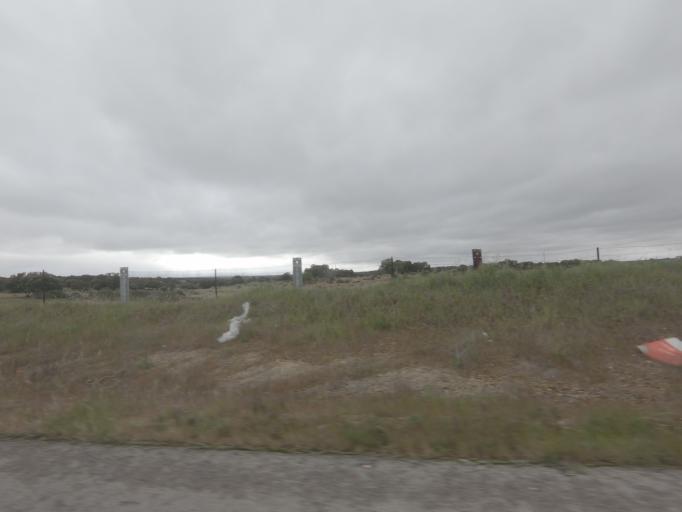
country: ES
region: Extremadura
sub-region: Provincia de Caceres
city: Caceres
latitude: 39.4037
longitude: -6.4209
